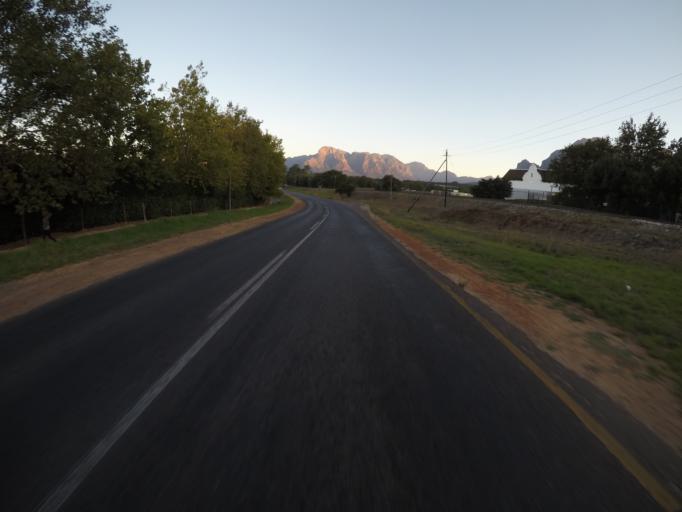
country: ZA
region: Western Cape
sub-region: Cape Winelands District Municipality
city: Paarl
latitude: -33.8369
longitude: 18.9540
